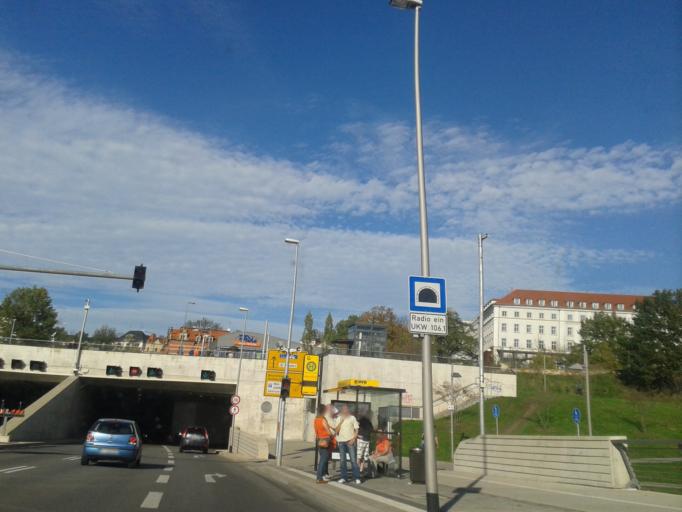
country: DE
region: Saxony
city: Albertstadt
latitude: 51.0664
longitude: 13.7767
